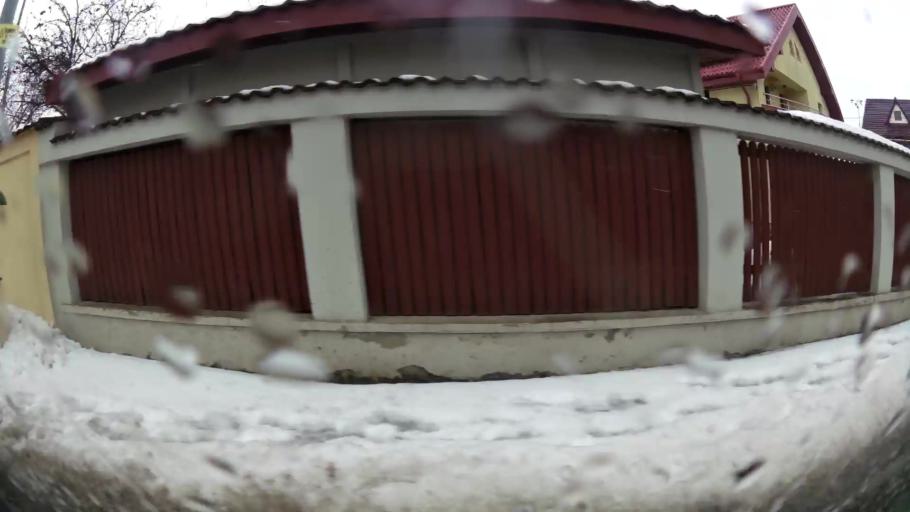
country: RO
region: Ilfov
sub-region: Comuna Chiajna
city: Rosu
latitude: 44.4066
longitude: 26.0115
